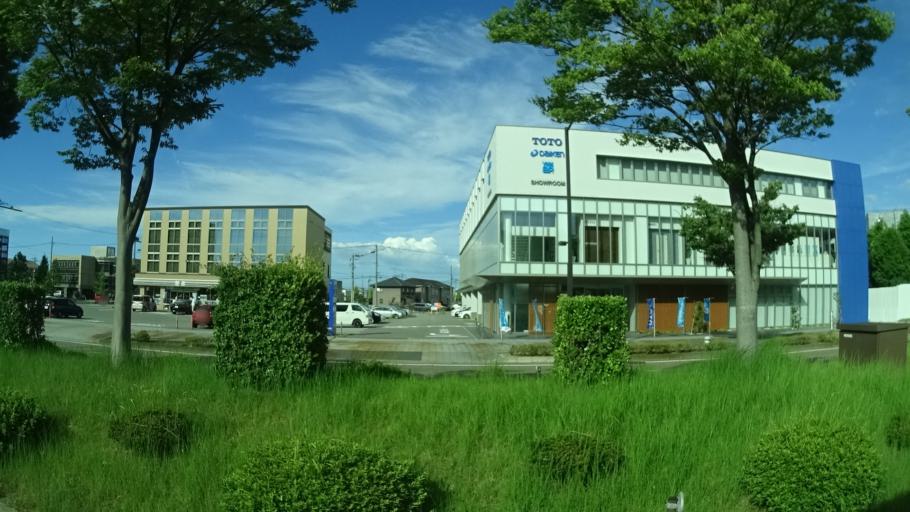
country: JP
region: Ishikawa
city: Kanazawa-shi
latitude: 36.5958
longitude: 136.6263
